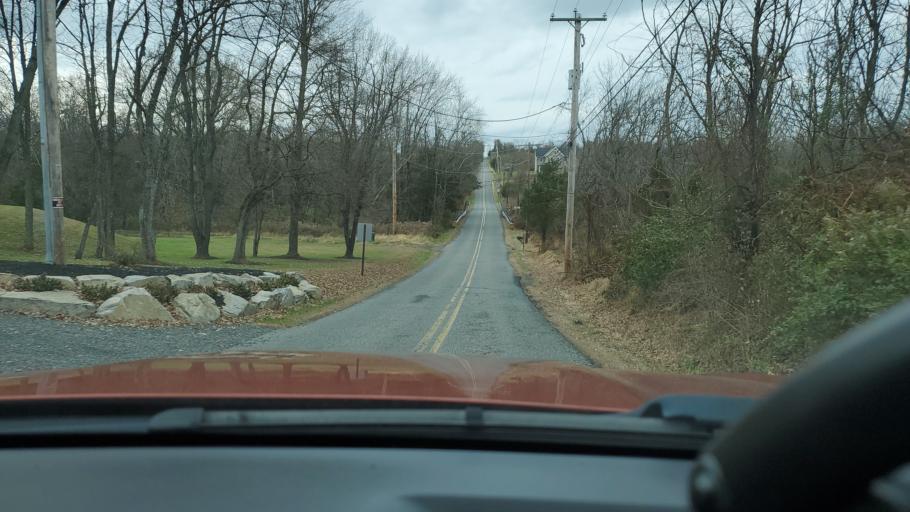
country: US
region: Pennsylvania
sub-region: Montgomery County
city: Spring Mount
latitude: 40.2932
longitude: -75.5062
